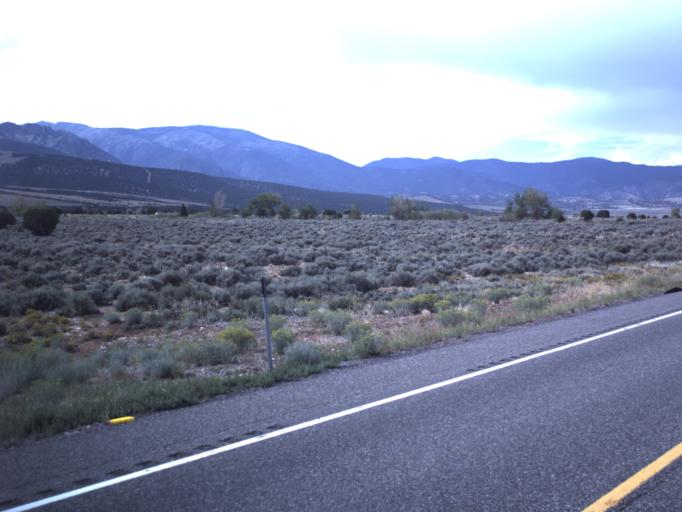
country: US
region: Utah
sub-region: Piute County
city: Junction
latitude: 38.3823
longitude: -112.2285
